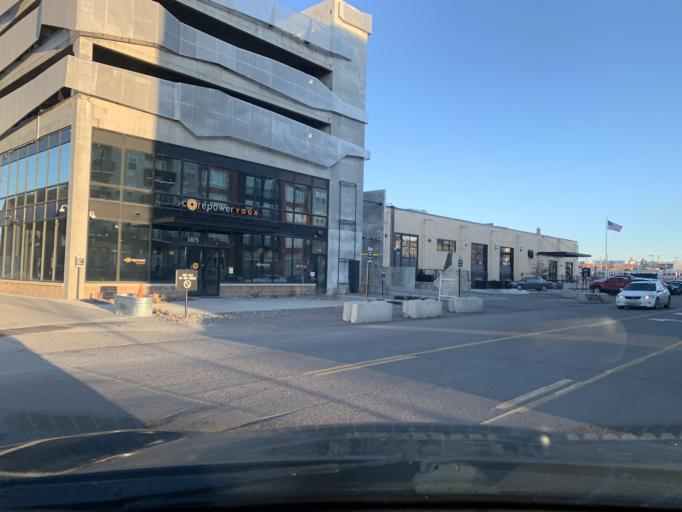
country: US
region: Colorado
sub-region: Denver County
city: Denver
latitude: 39.7650
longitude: -104.9875
